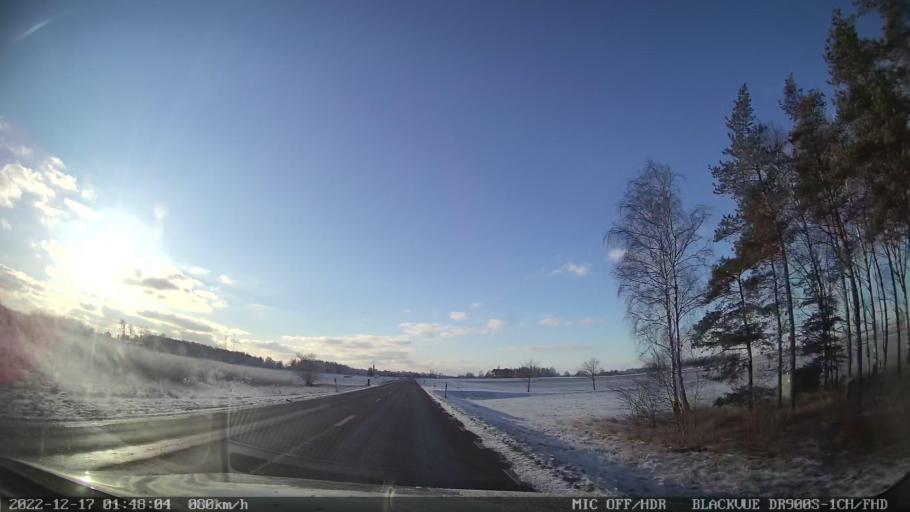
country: SE
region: Skane
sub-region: Tomelilla Kommun
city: Tomelilla
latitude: 55.5465
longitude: 14.0580
